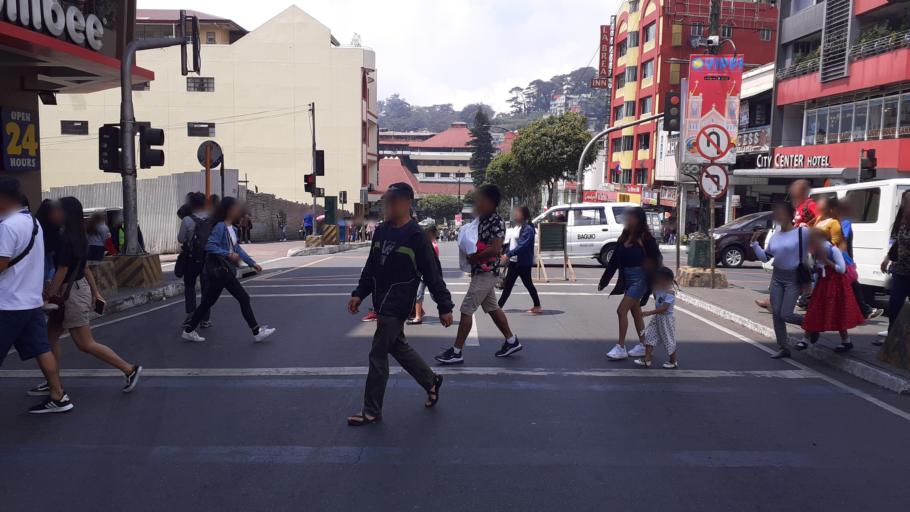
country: PH
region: Cordillera
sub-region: Baguio City
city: Baguio
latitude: 16.4131
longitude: 120.5967
